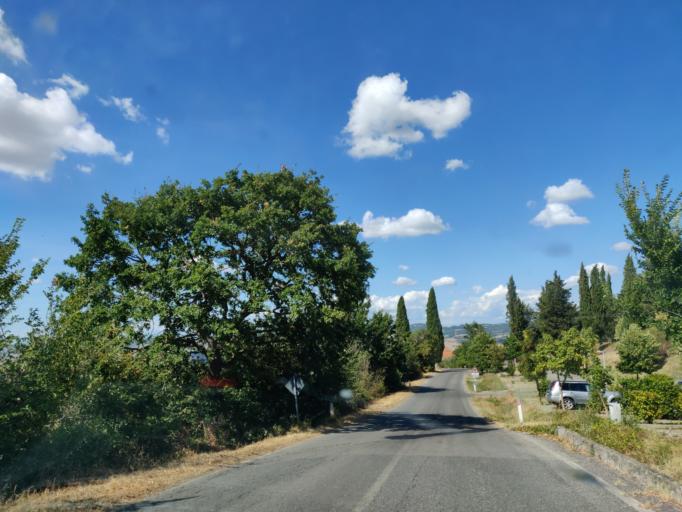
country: IT
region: Tuscany
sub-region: Provincia di Siena
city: Radicofani
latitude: 42.9725
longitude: 11.7371
